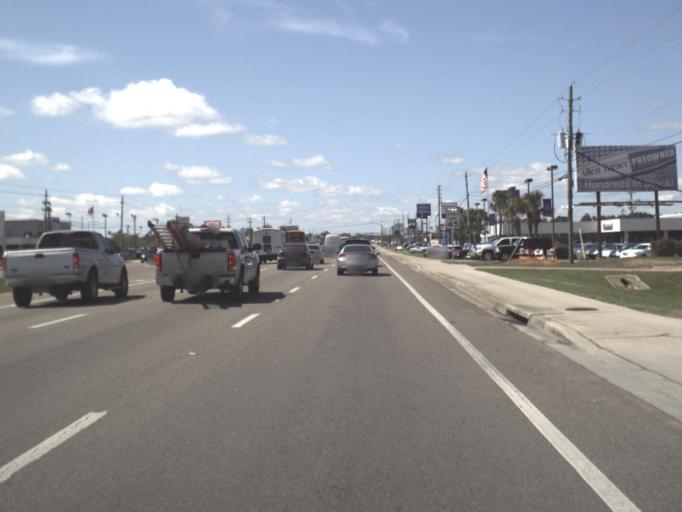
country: US
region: Florida
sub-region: Escambia County
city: Brent
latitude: 30.4751
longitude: -87.2487
